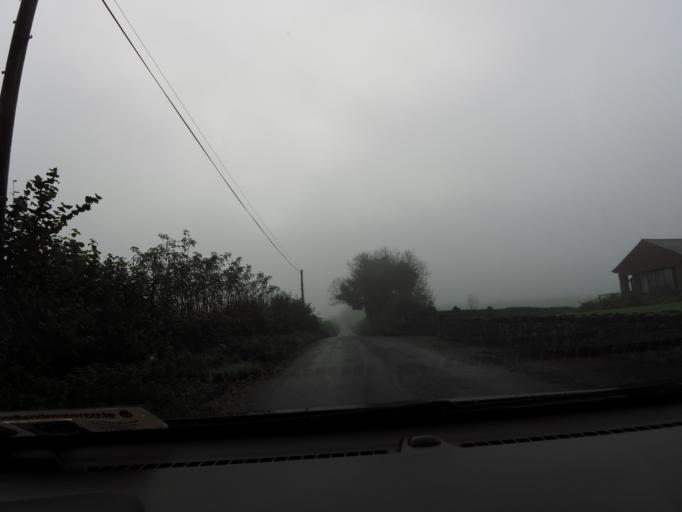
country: IE
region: Leinster
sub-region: An Iarmhi
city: Moate
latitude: 53.3899
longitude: -7.8081
